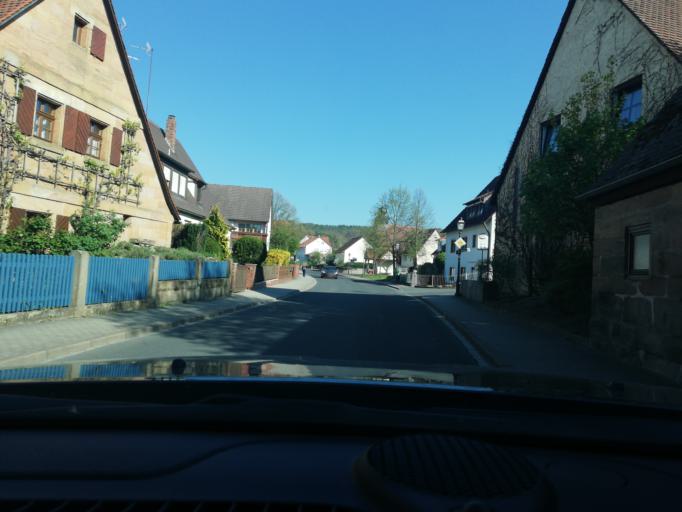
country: DE
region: Bavaria
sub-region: Regierungsbezirk Mittelfranken
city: Bubenreuth
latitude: 49.6273
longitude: 11.0174
